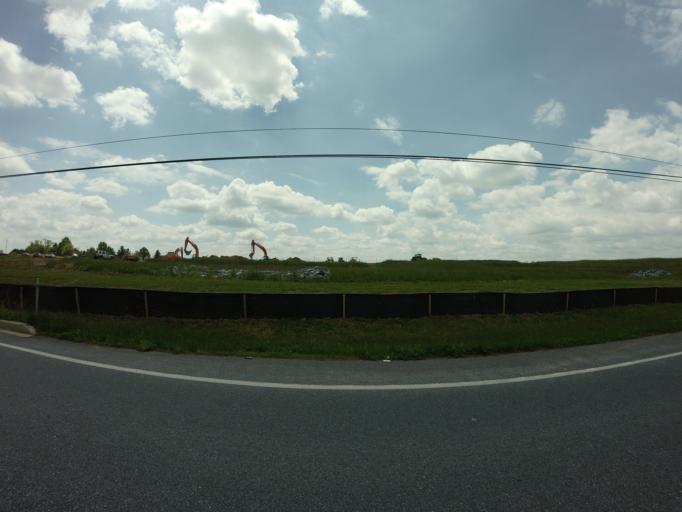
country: US
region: Maryland
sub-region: Frederick County
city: Urbana
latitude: 39.3309
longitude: -77.3610
